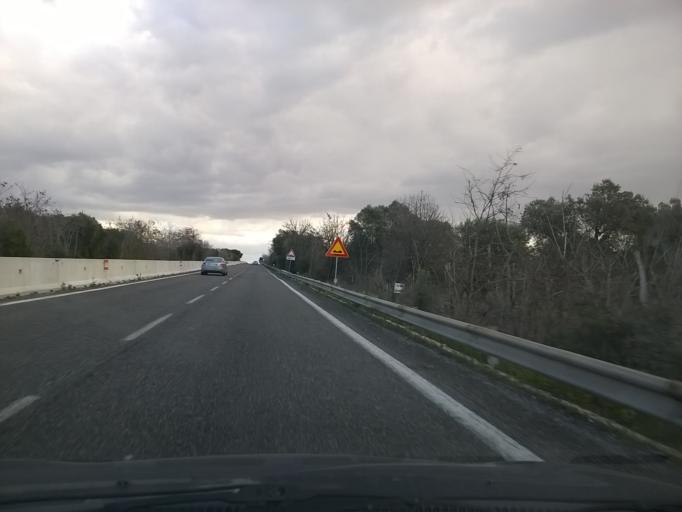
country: IT
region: Apulia
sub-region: Provincia di Taranto
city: Paolo VI
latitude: 40.5091
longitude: 17.2793
